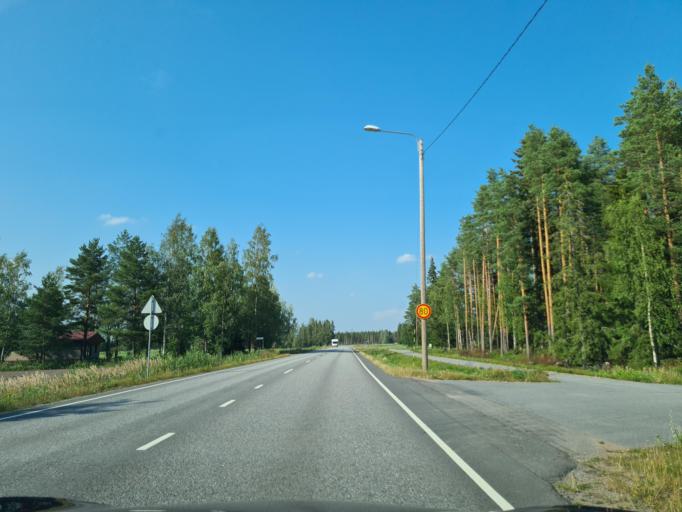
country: FI
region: Satakunta
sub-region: Pohjois-Satakunta
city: Karvia
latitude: 62.0897
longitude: 22.5273
